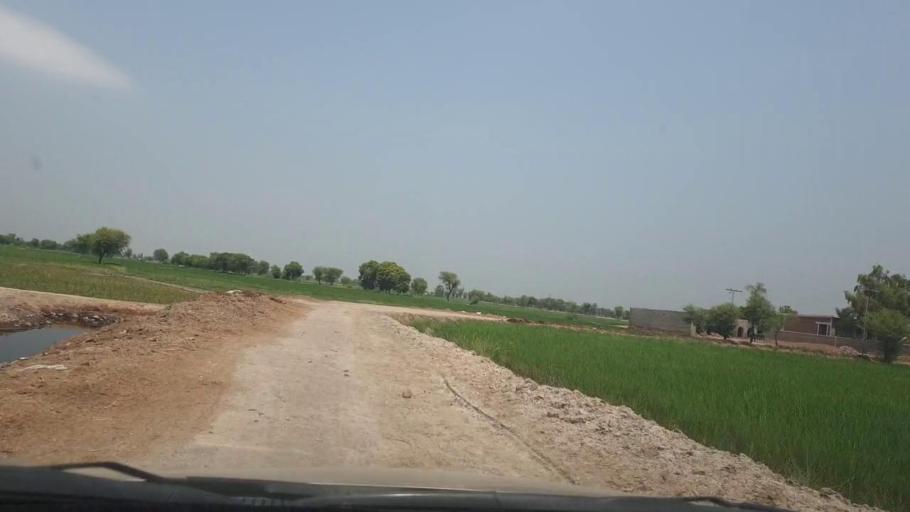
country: PK
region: Sindh
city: Ratodero
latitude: 27.7290
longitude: 68.2949
